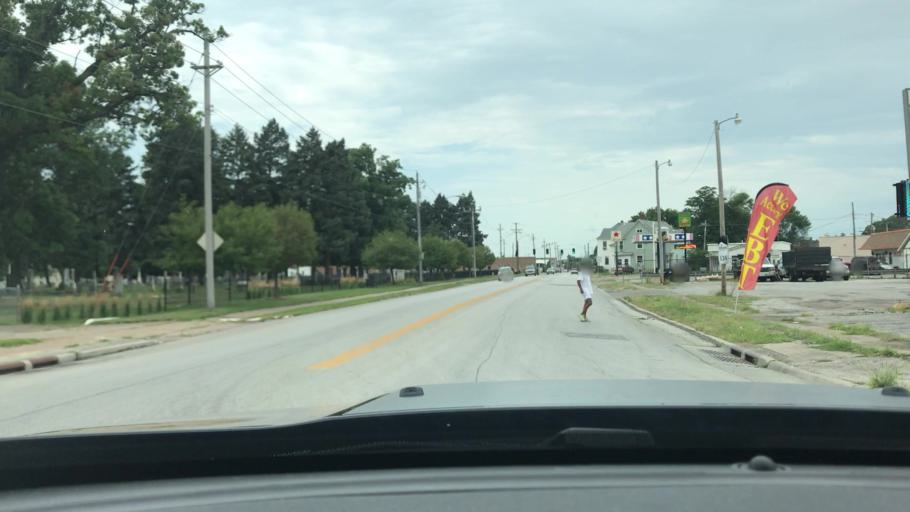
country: US
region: Iowa
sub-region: Scott County
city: Davenport
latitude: 41.5205
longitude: -90.5989
